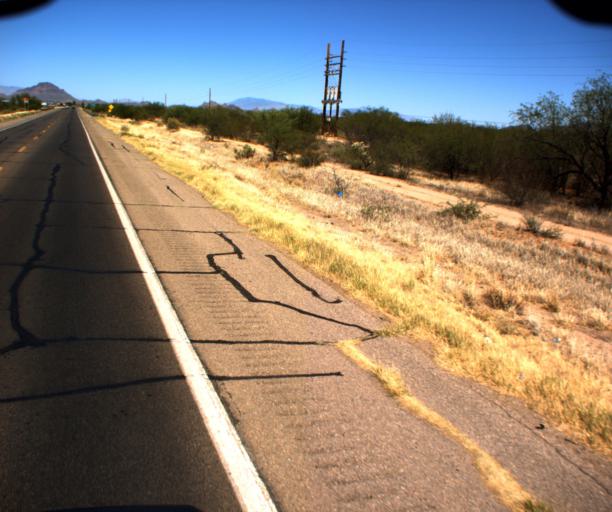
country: US
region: Arizona
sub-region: Pima County
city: Valencia West
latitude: 32.1286
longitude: -111.1868
